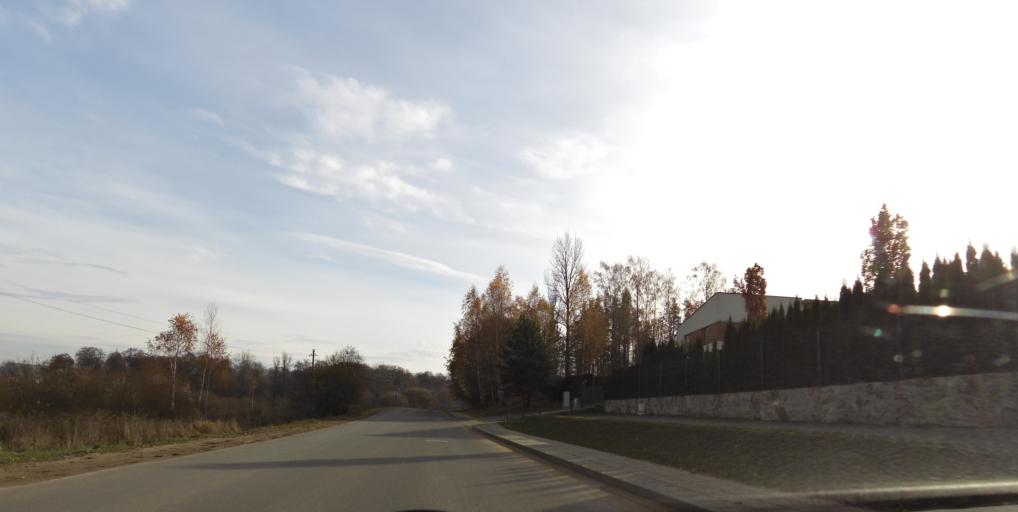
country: LT
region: Vilnius County
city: Pilaite
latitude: 54.7223
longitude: 25.1919
